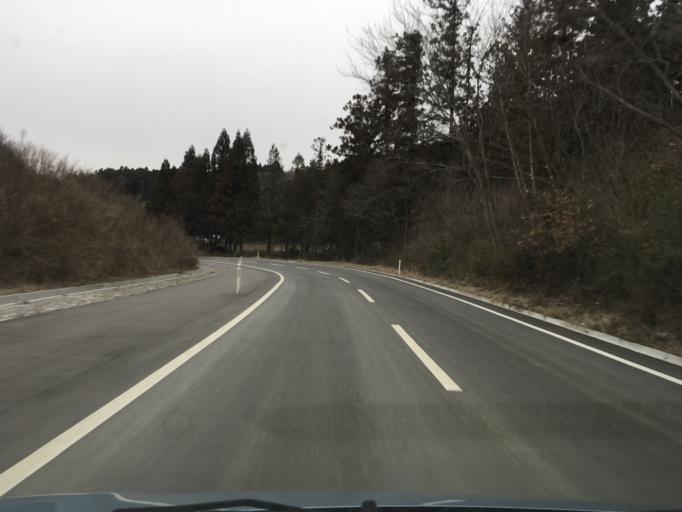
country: JP
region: Miyagi
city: Wakuya
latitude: 38.6697
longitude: 141.2769
